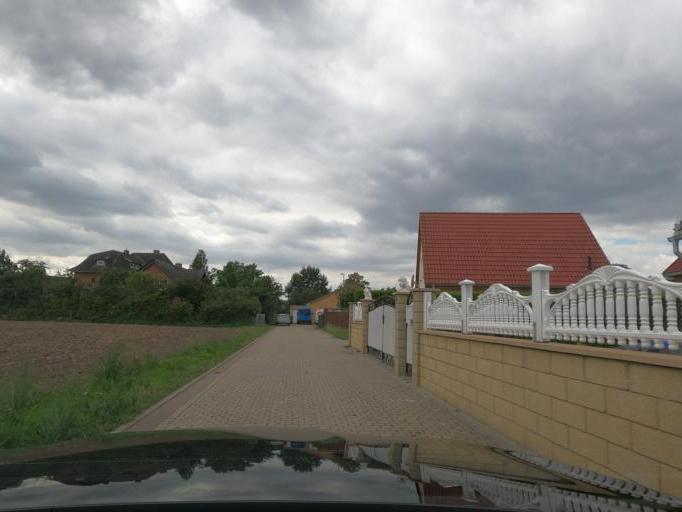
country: DE
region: Lower Saxony
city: Sehnde
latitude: 52.3512
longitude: 9.8992
